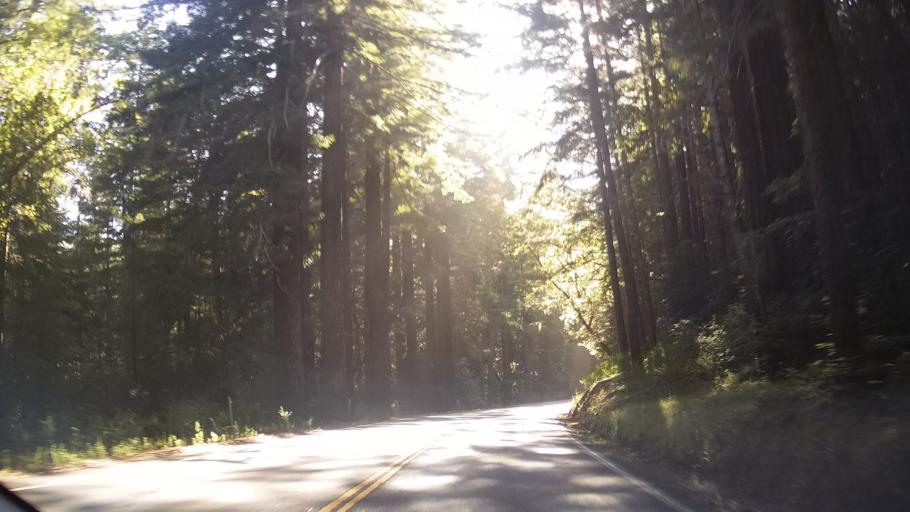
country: US
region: California
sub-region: Mendocino County
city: Brooktrails
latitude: 39.3466
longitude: -123.5640
